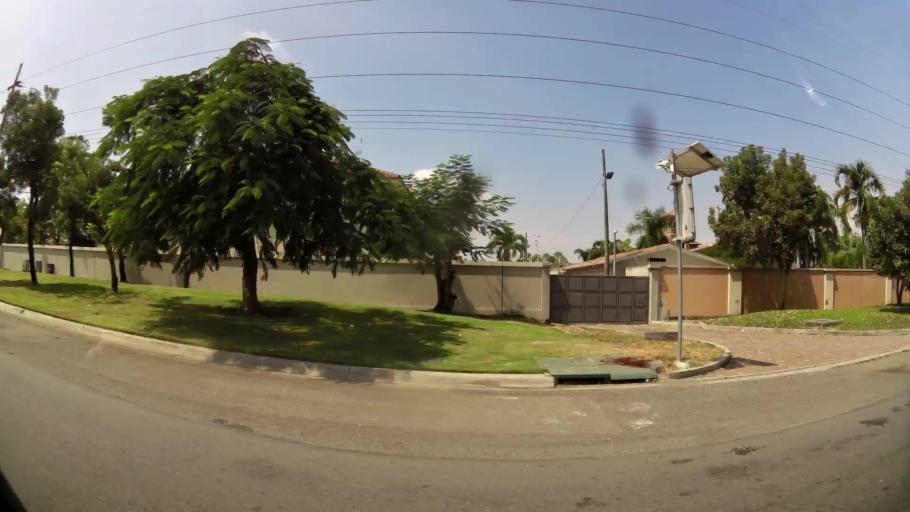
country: EC
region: Guayas
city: Eloy Alfaro
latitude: -2.0888
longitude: -79.8734
